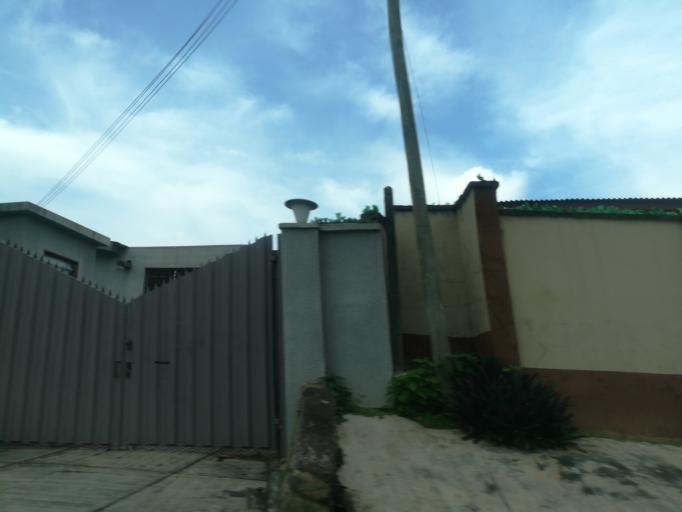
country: NG
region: Oyo
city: Ibadan
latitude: 7.4145
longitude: 3.9011
